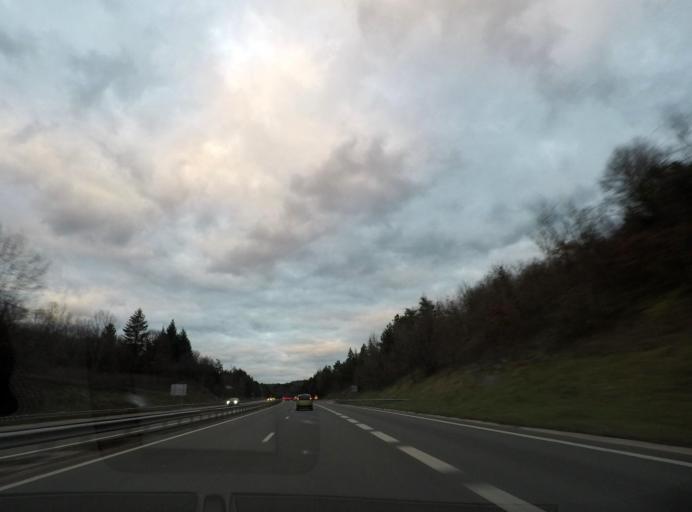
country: FR
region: Rhone-Alpes
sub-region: Departement de l'Ain
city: Poncin
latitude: 46.1095
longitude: 5.4626
